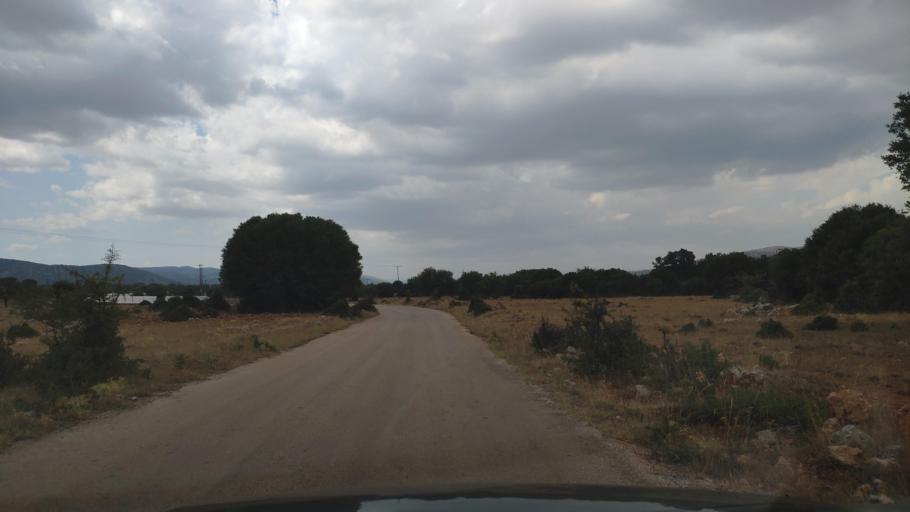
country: GR
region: Peloponnese
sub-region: Nomos Lakonias
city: Kariai
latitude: 37.3101
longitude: 22.4527
